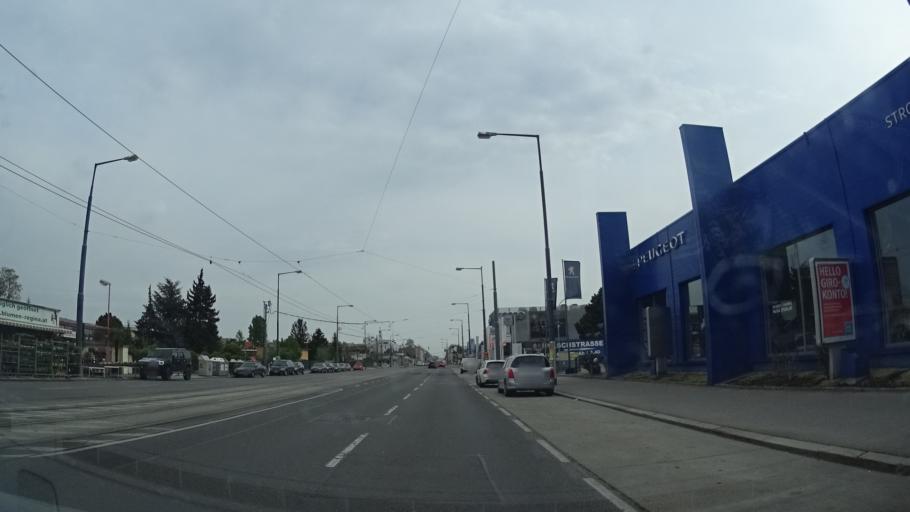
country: AT
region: Lower Austria
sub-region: Politischer Bezirk Korneuburg
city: Langenzersdorf
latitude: 48.2751
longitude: 16.3890
